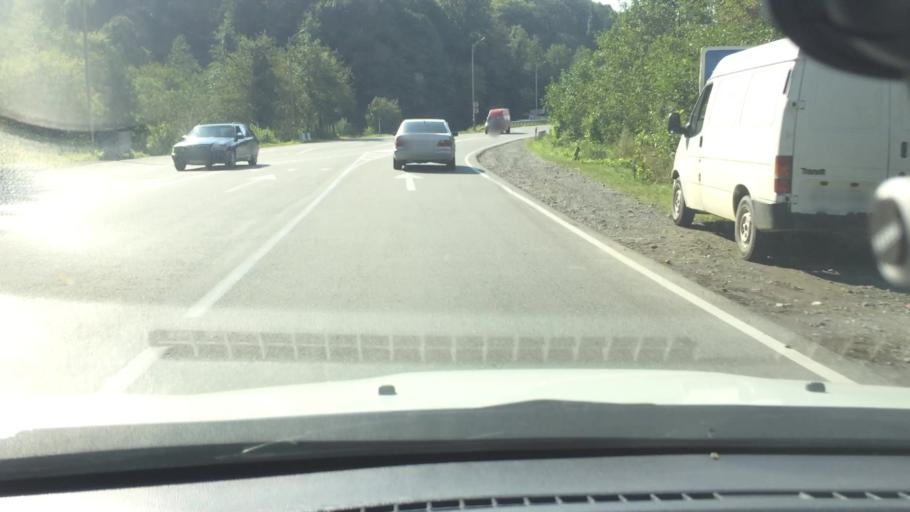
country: GE
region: Guria
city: Urek'i
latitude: 41.9706
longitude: 41.7822
